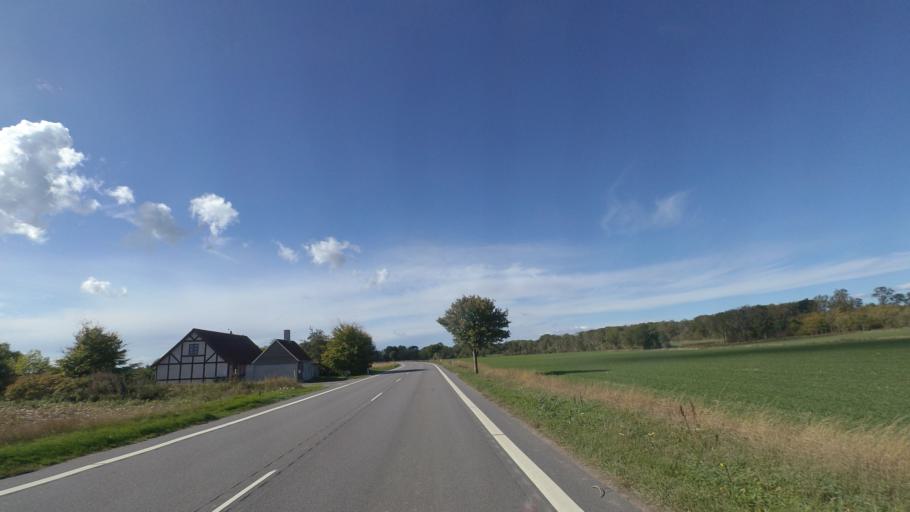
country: DK
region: Capital Region
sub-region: Bornholm Kommune
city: Ronne
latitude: 55.0736
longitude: 14.7983
